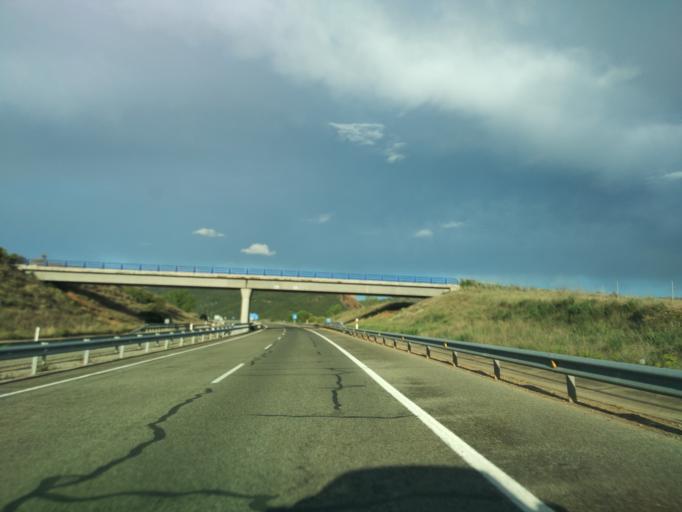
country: ES
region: Castille-La Mancha
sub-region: Provincia de Guadalajara
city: Guadalajara
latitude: 40.6593
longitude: -3.1353
